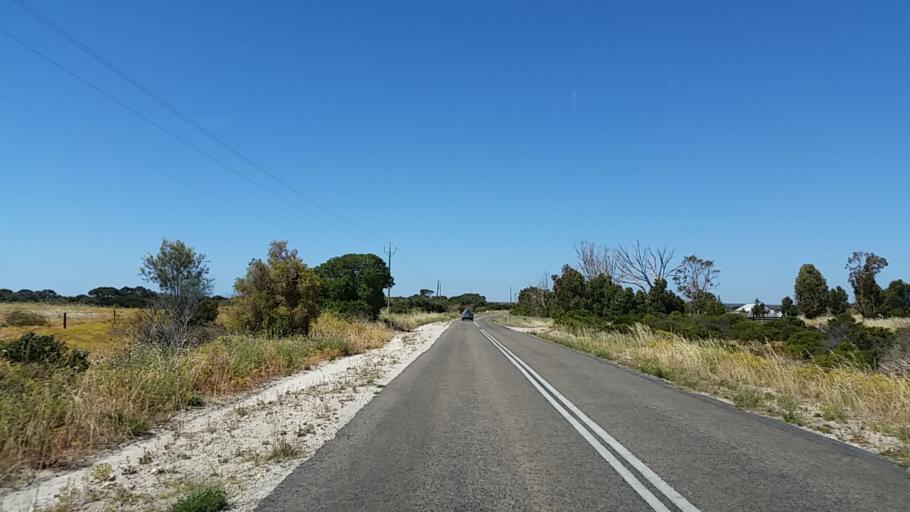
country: AU
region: South Australia
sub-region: Yorke Peninsula
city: Honiton
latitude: -35.2266
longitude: 136.9877
